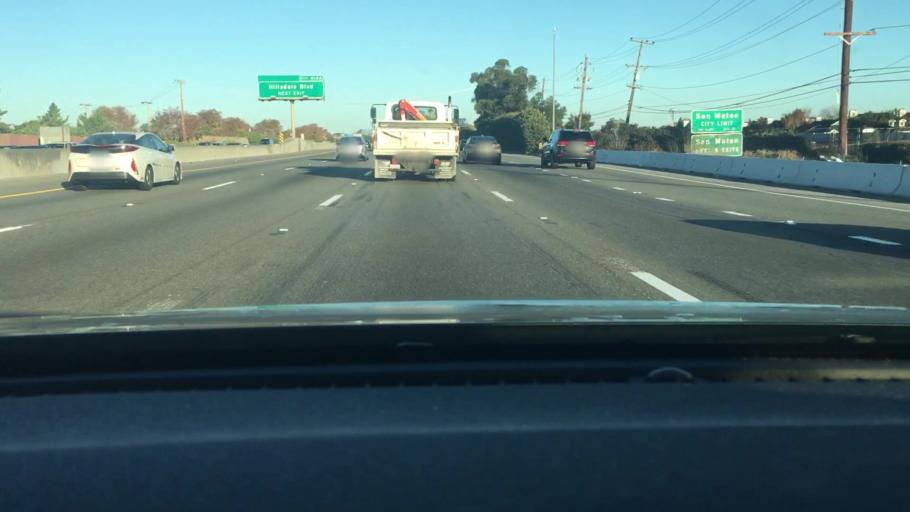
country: US
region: California
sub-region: San Mateo County
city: Belmont
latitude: 37.5330
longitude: -122.2764
